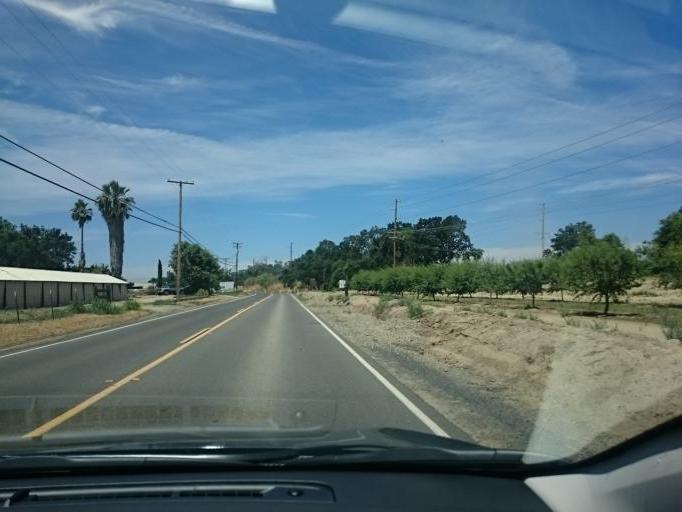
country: US
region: California
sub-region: Stanislaus County
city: Waterford
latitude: 37.6420
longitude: -120.6376
